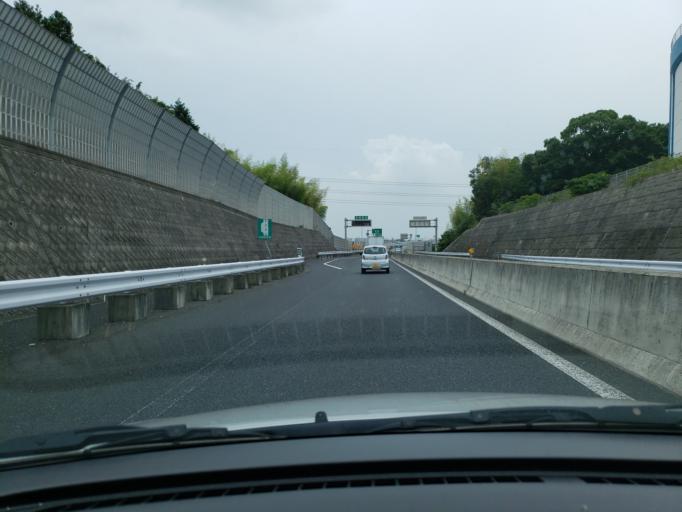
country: JP
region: Hyogo
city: Kakogawacho-honmachi
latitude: 34.7706
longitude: 134.8857
